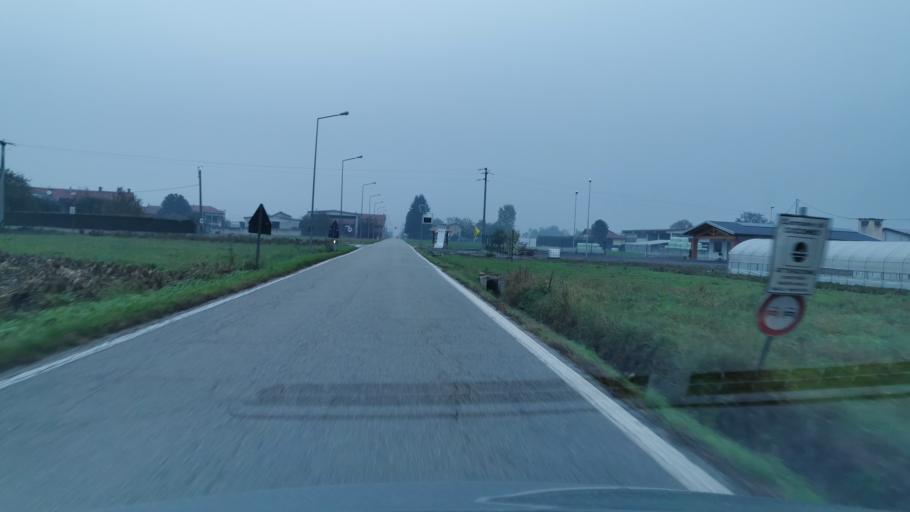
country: IT
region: Piedmont
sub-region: Provincia di Torino
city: Ciconio
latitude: 45.3263
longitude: 7.7611
